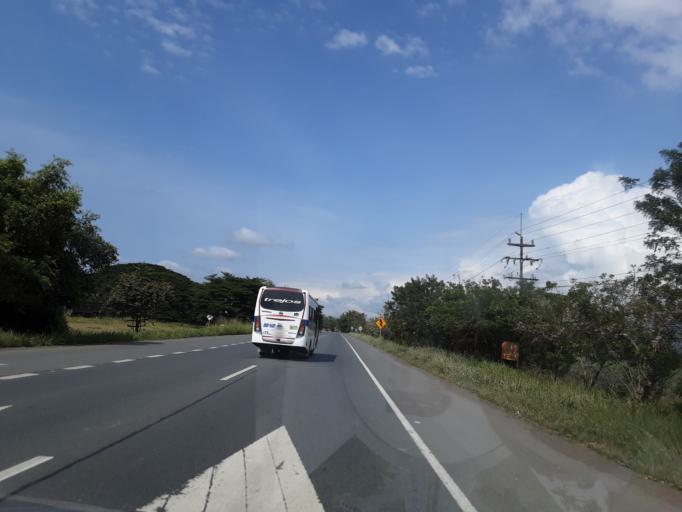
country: CO
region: Valle del Cauca
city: Guacari
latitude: 3.7846
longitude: -76.3219
